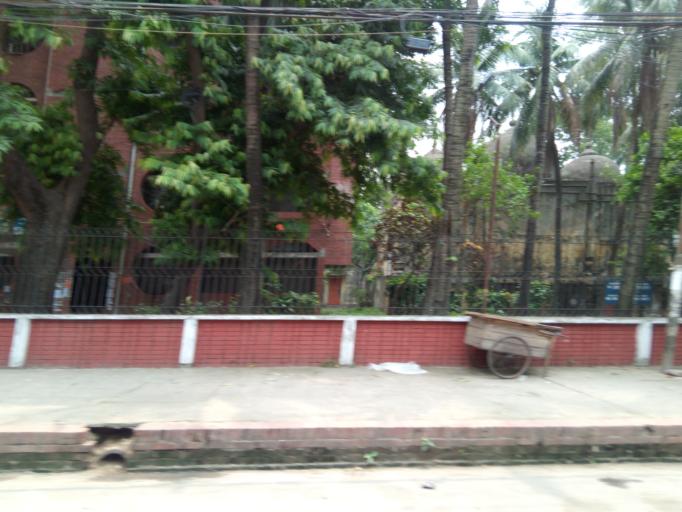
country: BD
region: Dhaka
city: Azimpur
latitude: 23.7270
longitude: 90.4005
